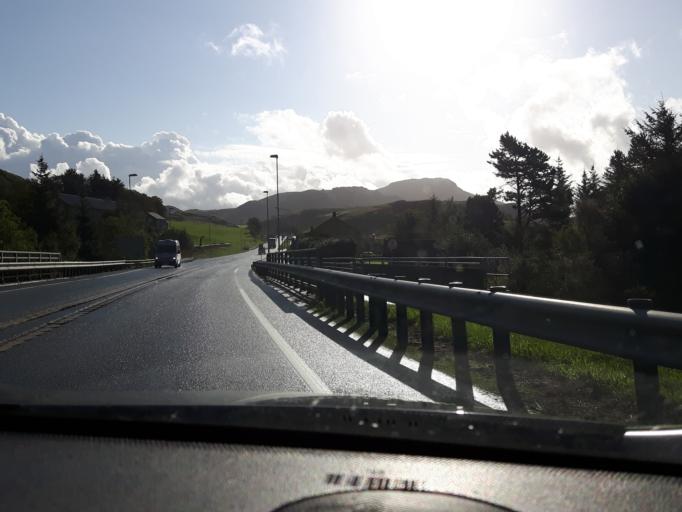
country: NO
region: Rogaland
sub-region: Gjesdal
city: Algard
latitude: 58.7656
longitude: 5.8834
